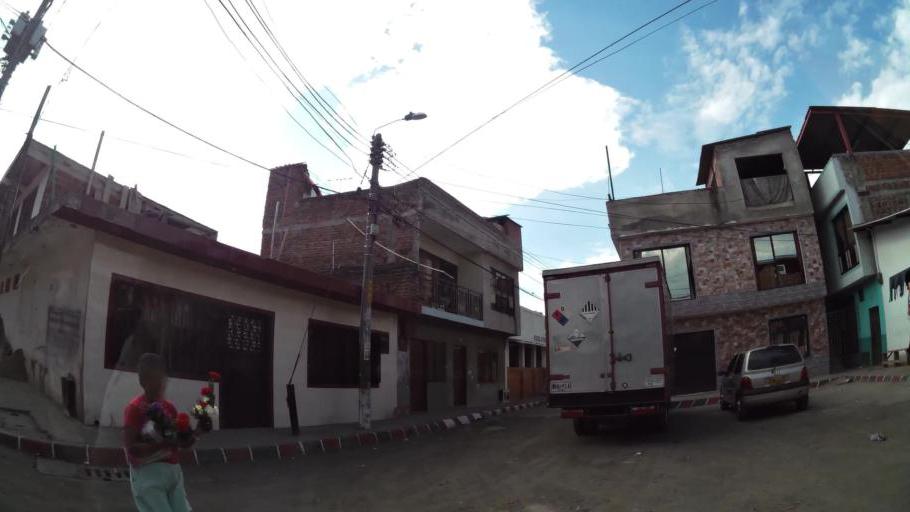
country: CO
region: Valle del Cauca
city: Cali
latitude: 3.4635
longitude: -76.5181
